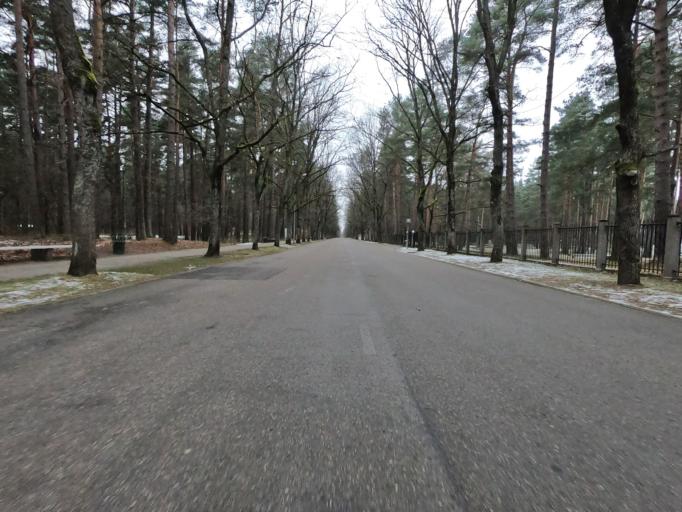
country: LV
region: Riga
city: Jaunciems
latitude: 57.0139
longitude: 24.1507
